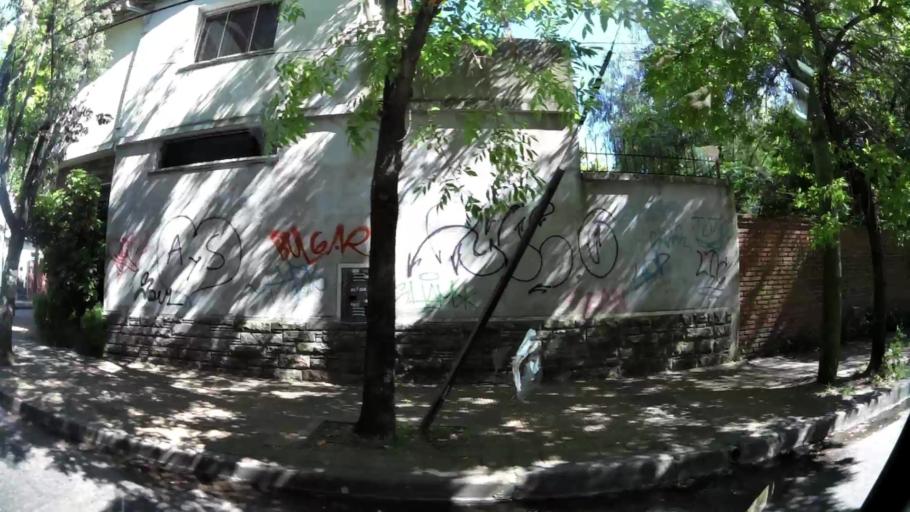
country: AR
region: Buenos Aires
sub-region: Partido de Vicente Lopez
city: Olivos
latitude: -34.5233
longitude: -58.4825
